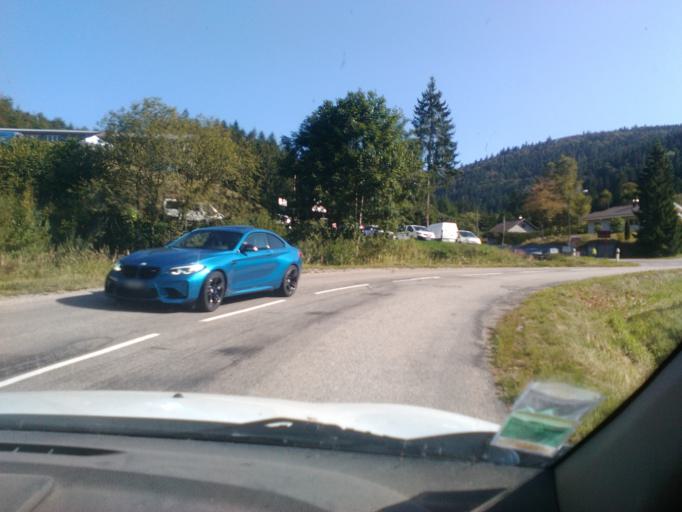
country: FR
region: Lorraine
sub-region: Departement des Vosges
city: Xonrupt-Longemer
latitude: 48.0353
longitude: 6.9243
